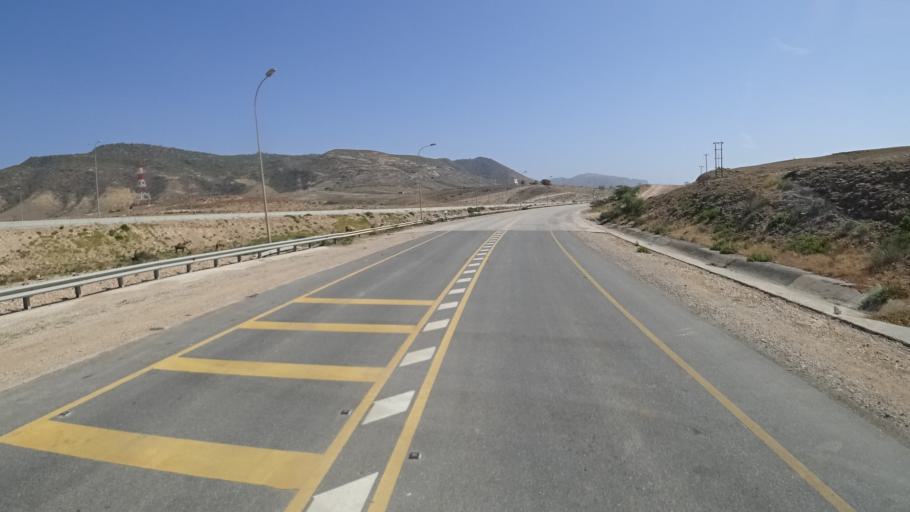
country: OM
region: Zufar
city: Salalah
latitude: 17.0589
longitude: 54.4330
